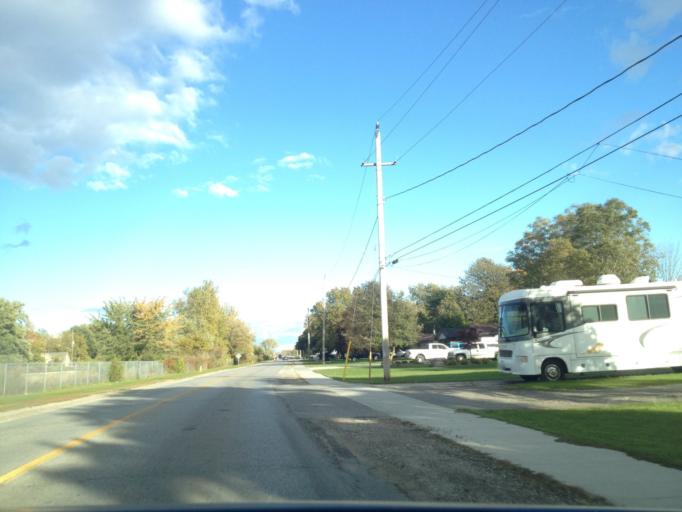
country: US
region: Michigan
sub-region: Wayne County
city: Grosse Pointe Farms
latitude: 42.2964
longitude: -82.6935
